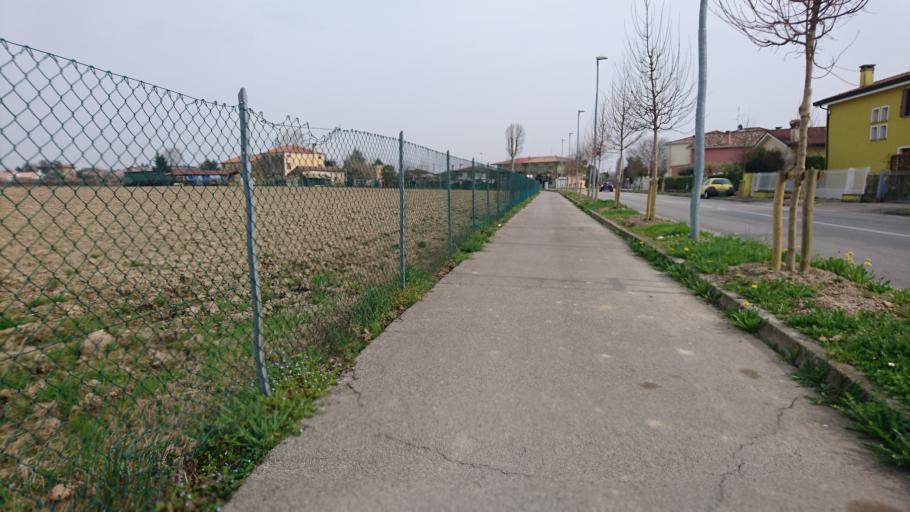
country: IT
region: Veneto
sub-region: Provincia di Padova
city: Selvazzano Dentro
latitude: 45.3805
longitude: 11.7661
